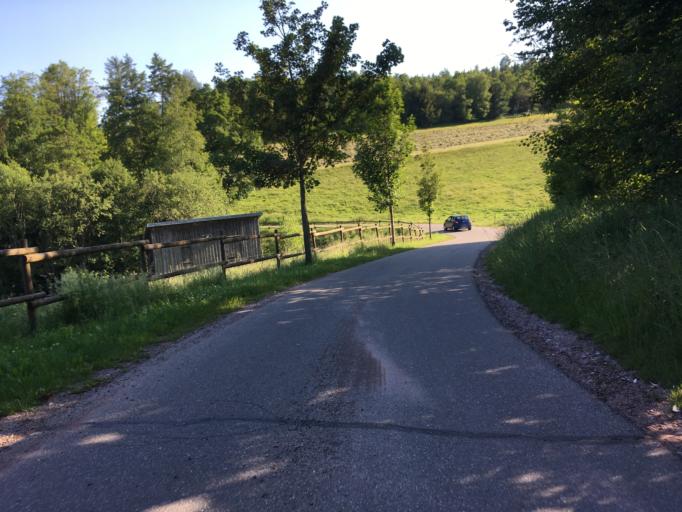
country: DE
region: Baden-Wuerttemberg
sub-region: Freiburg Region
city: Friedenweiler
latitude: 47.9226
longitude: 8.2555
